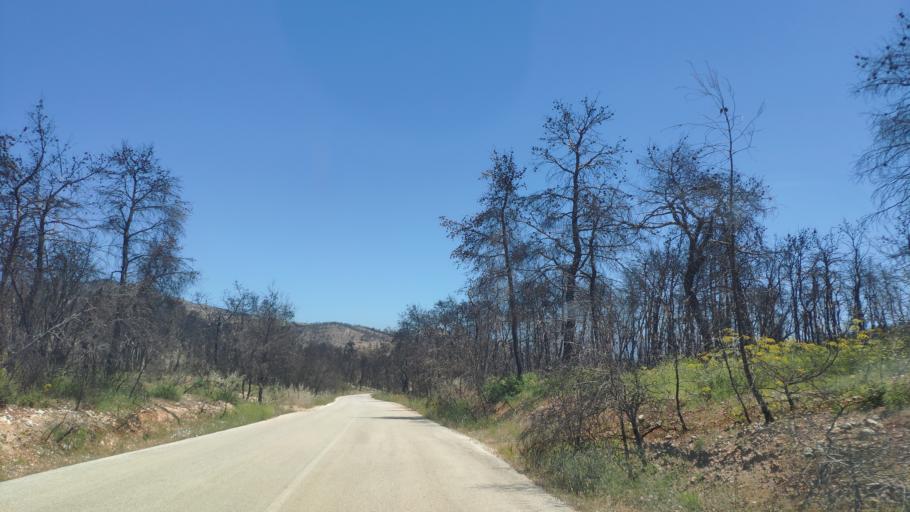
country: GR
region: Peloponnese
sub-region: Nomos Korinthias
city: Athikia
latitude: 37.8368
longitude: 22.9430
